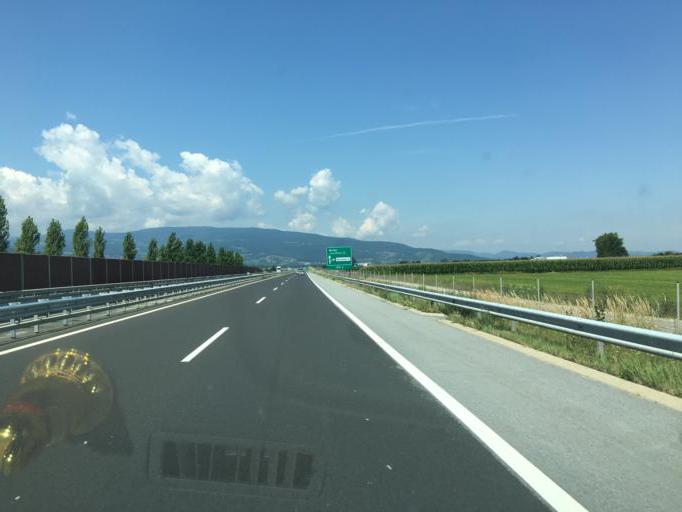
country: SI
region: Race-Fram
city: Race
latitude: 46.4657
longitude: 15.6925
